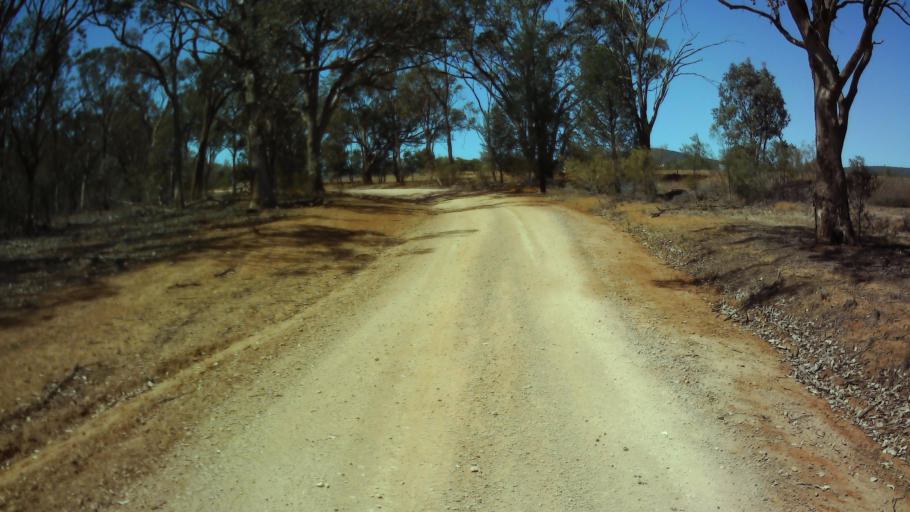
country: AU
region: New South Wales
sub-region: Weddin
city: Grenfell
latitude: -33.9423
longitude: 148.0788
